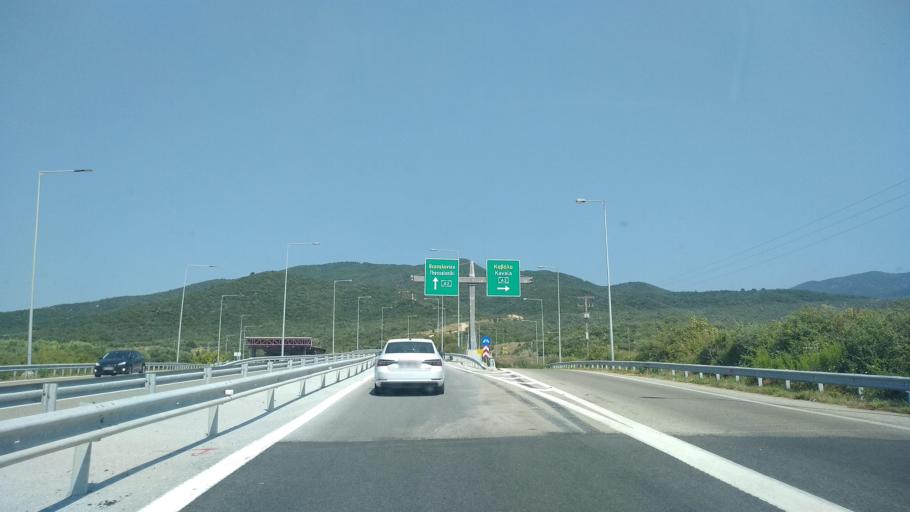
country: GR
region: Central Macedonia
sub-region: Nomos Thessalonikis
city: Nea Vrasna
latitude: 40.7088
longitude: 23.6843
